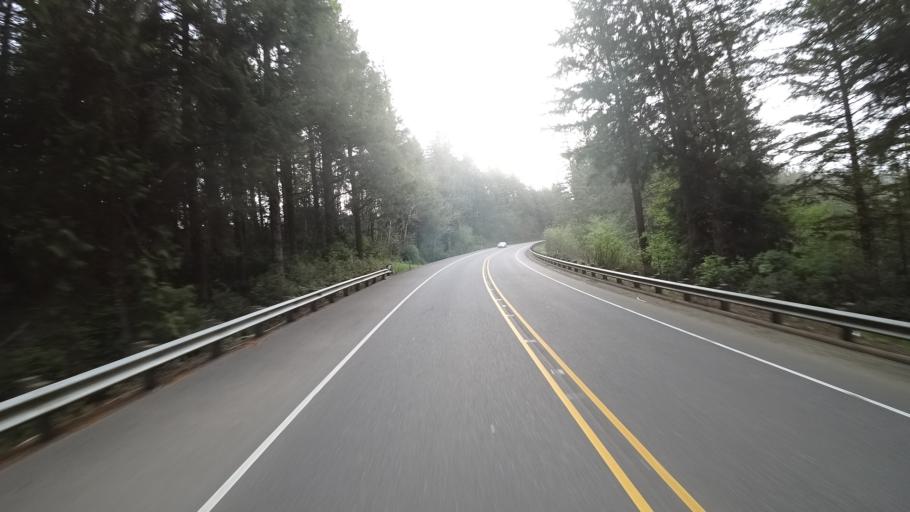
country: US
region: Oregon
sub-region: Coos County
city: Barview
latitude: 43.2552
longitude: -124.2830
